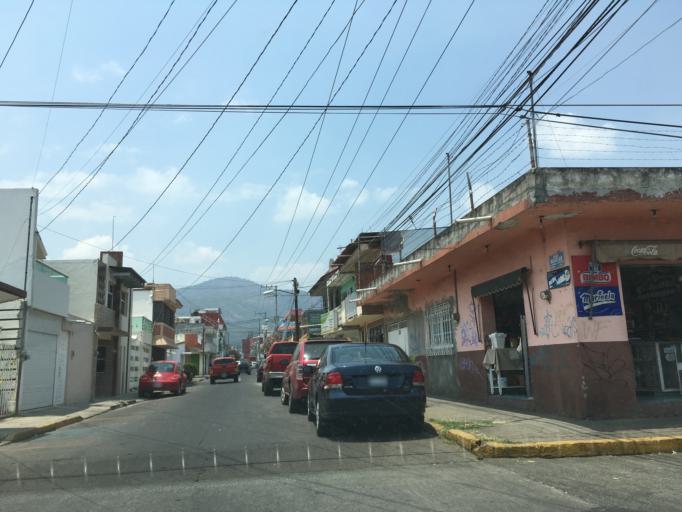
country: MX
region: Michoacan
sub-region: Uruapan
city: Uruapan
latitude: 19.4139
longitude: -102.0531
